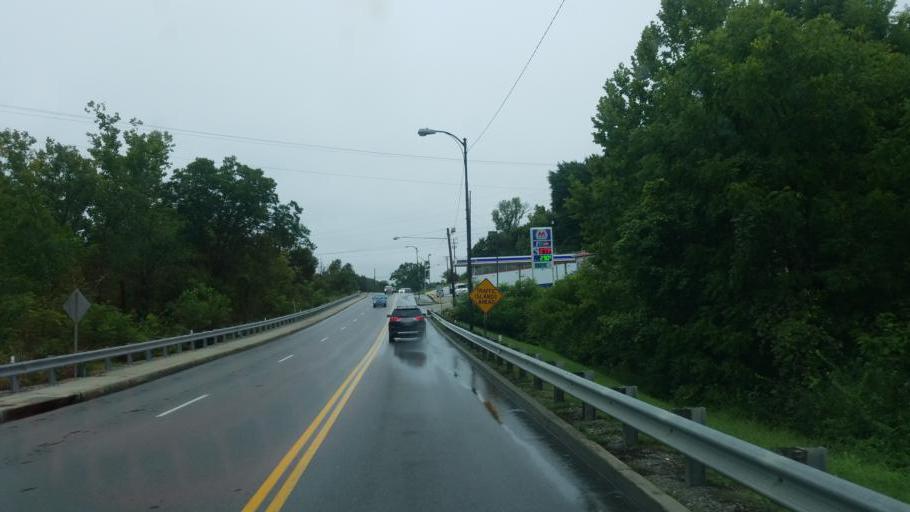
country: US
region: Kentucky
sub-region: Mason County
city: Maysville
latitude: 38.6424
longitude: -83.7579
